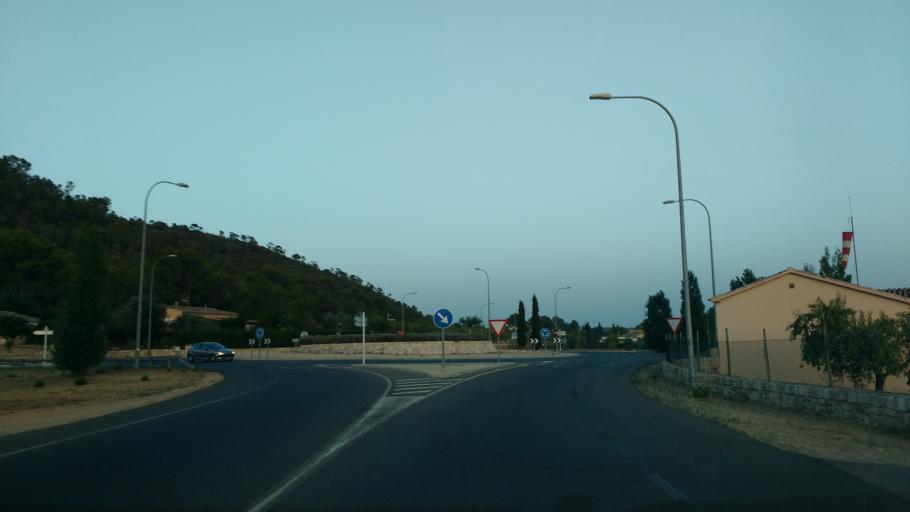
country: ES
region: Balearic Islands
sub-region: Illes Balears
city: Bunyola
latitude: 39.6666
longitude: 2.7127
